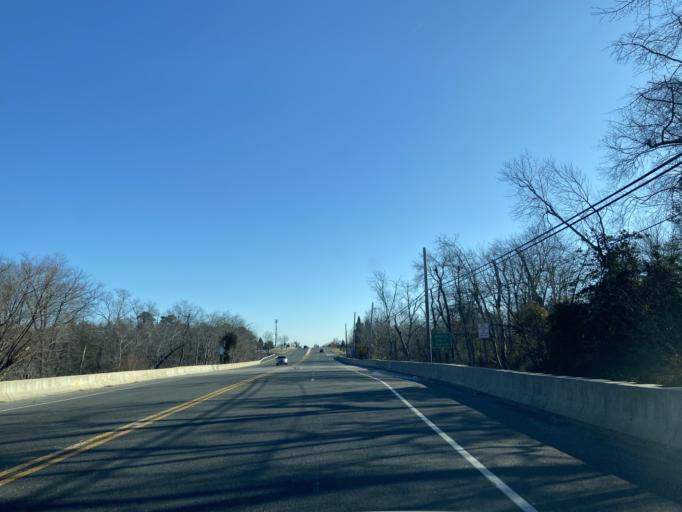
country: US
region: New Jersey
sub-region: Cumberland County
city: Vineland
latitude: 39.4885
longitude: -75.0760
